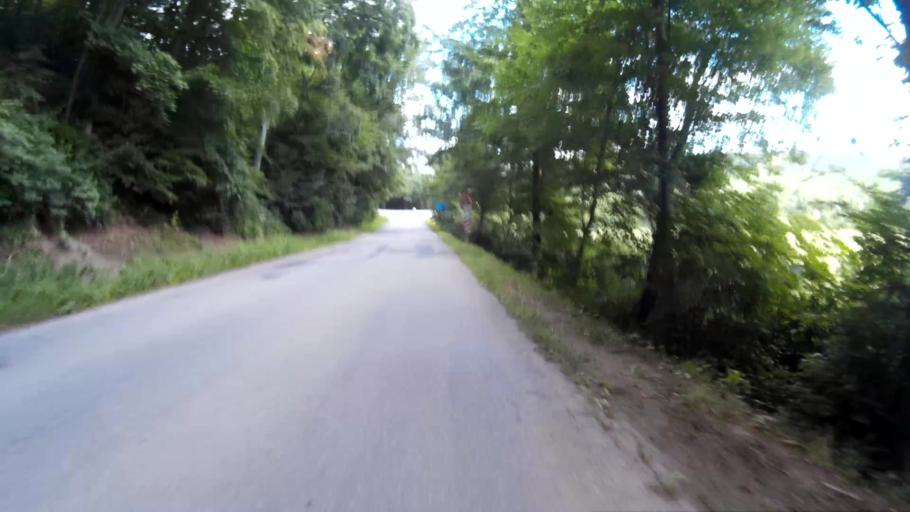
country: CZ
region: South Moravian
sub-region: Okres Brno-Venkov
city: Rosice
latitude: 49.1640
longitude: 16.4398
